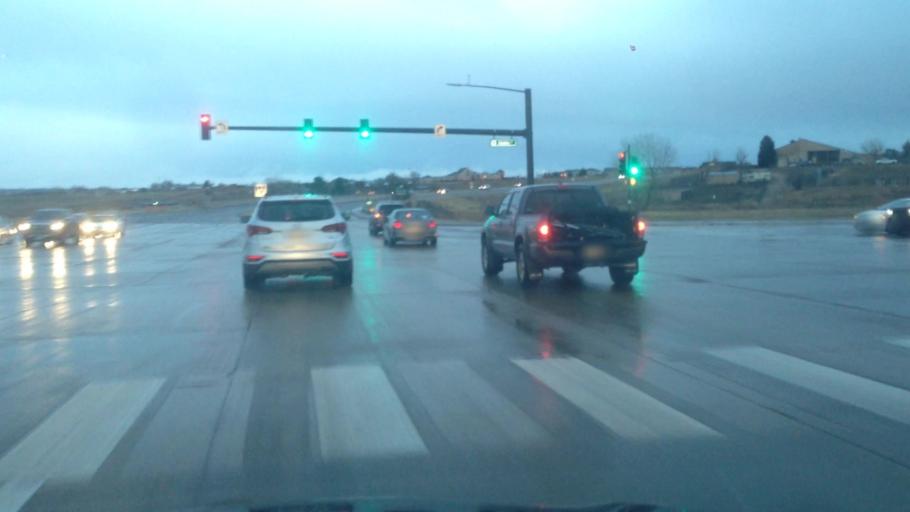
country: US
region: Colorado
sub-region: Douglas County
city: Stonegate
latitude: 39.5171
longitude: -104.8136
